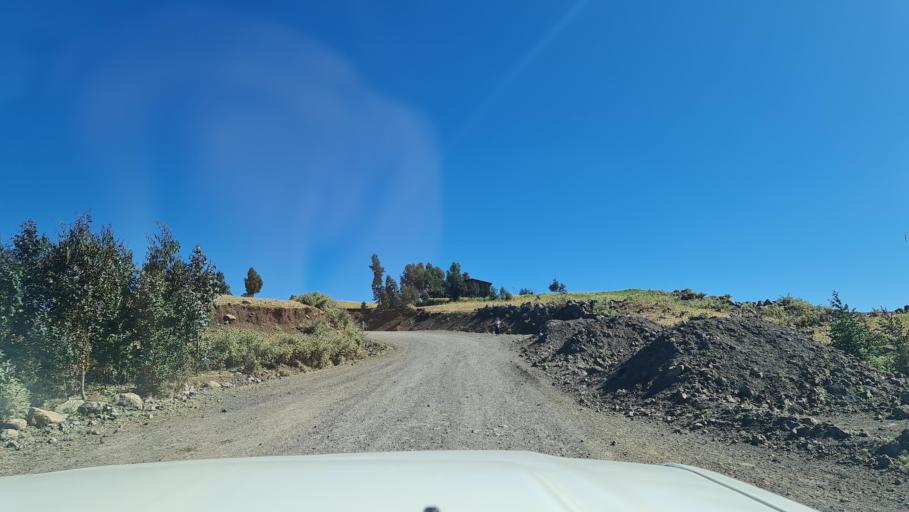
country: ET
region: Amhara
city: Debark'
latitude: 13.1162
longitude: 38.1540
